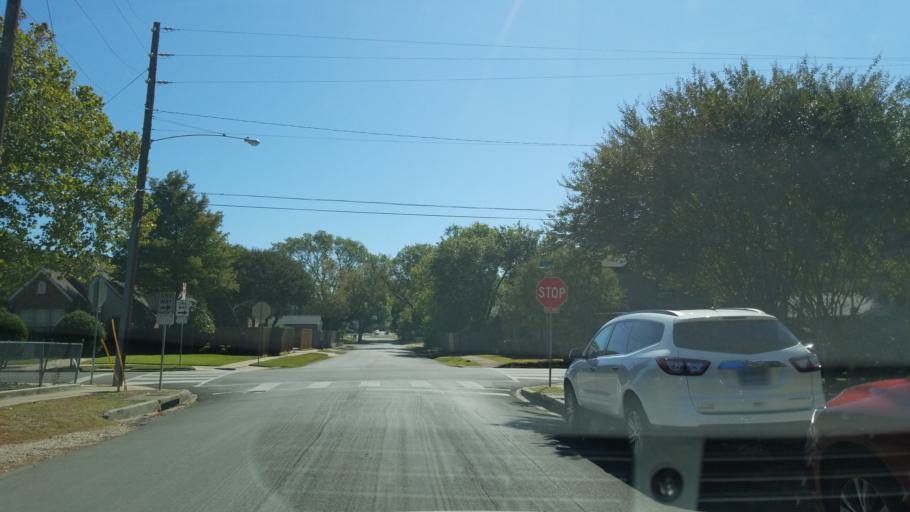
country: US
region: Texas
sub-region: Dallas County
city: Highland Park
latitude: 32.8065
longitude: -96.7575
